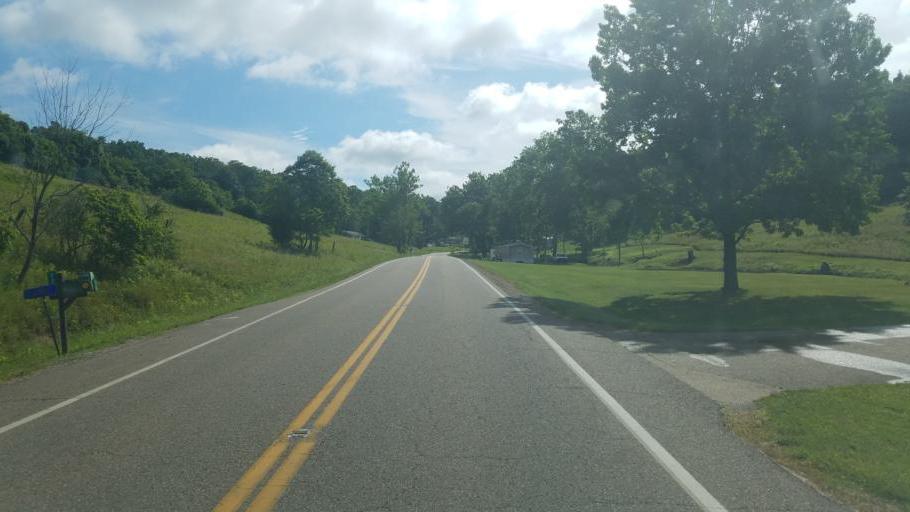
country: US
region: Ohio
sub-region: Gallia County
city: Gallipolis
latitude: 38.8237
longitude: -82.2485
